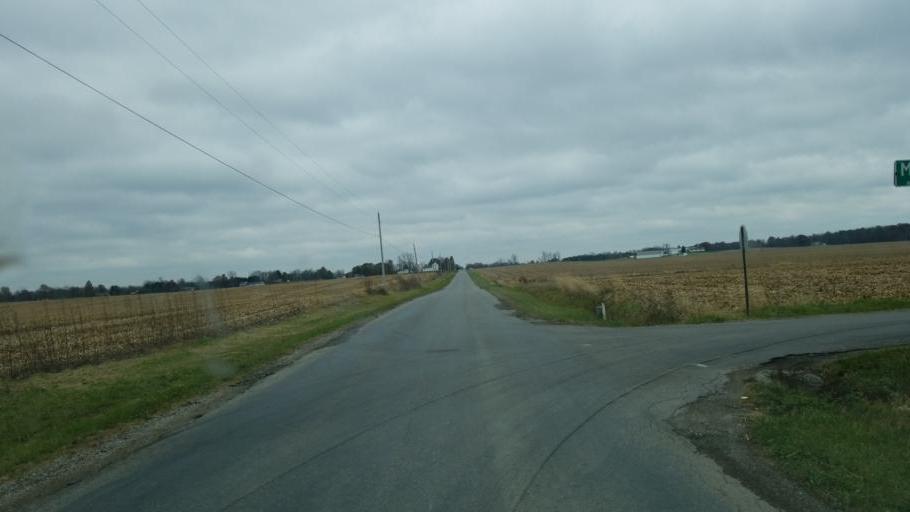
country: US
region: Ohio
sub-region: Licking County
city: Johnstown
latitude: 40.1636
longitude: -82.7590
